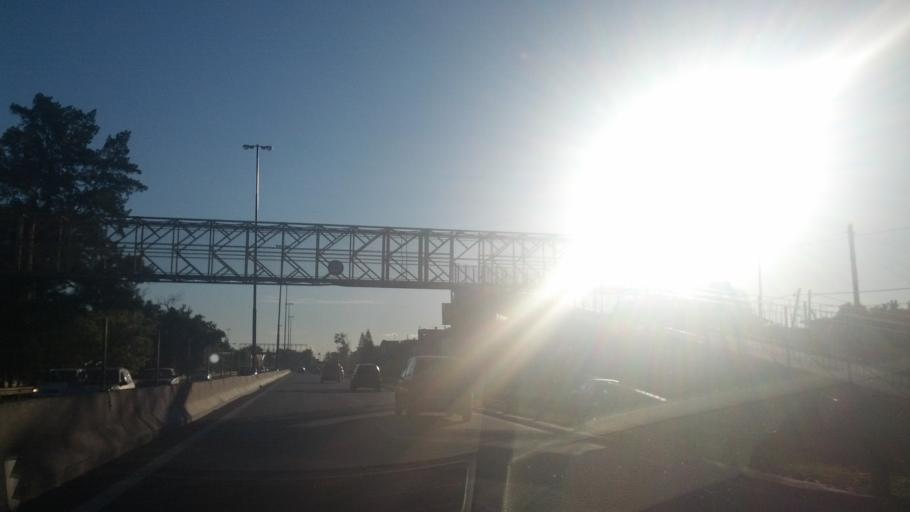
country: AR
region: Buenos Aires
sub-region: Partido de Lomas de Zamora
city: Lomas de Zamora
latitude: -34.7495
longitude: -58.4328
